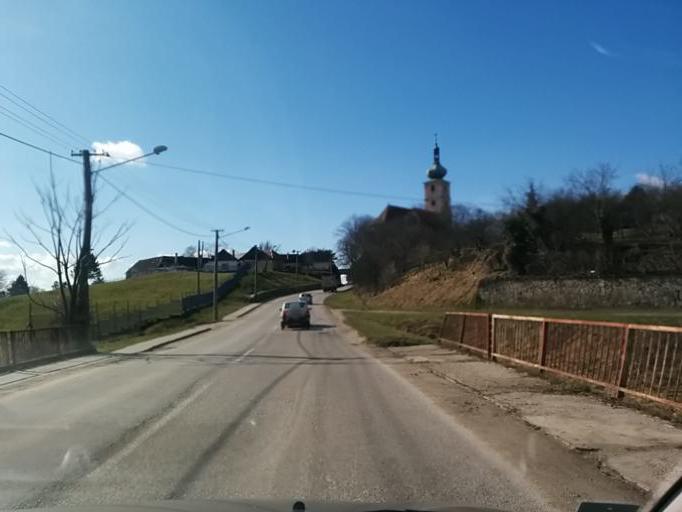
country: SK
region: Nitriansky
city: Cachtice
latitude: 48.7171
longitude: 17.7887
